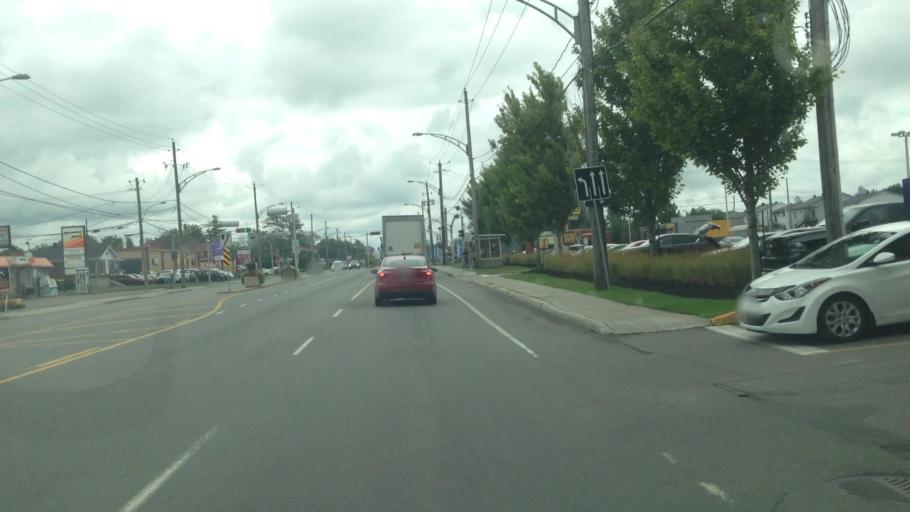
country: CA
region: Quebec
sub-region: Laurentides
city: Blainville
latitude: 45.6997
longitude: -73.9209
